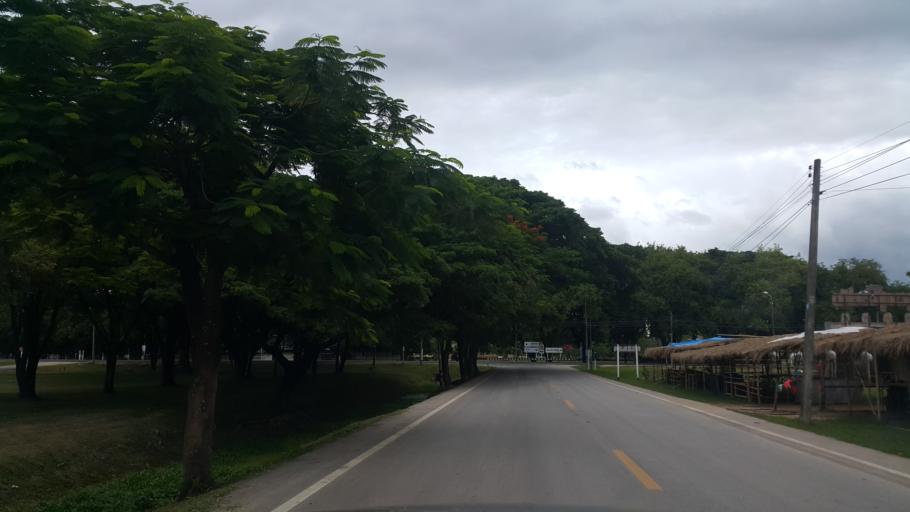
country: TH
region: Sukhothai
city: Ban Na
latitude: 17.0221
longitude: 99.7041
